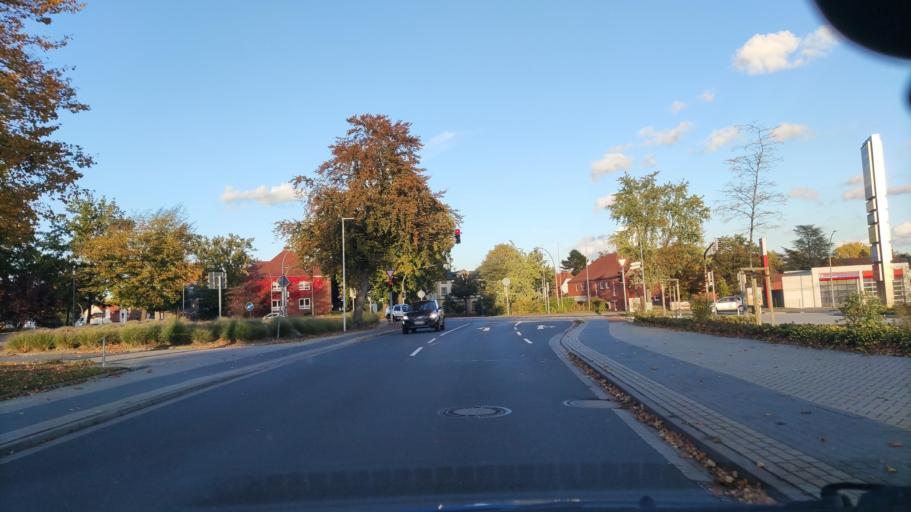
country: DE
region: Lower Saxony
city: Munster
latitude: 52.9893
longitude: 10.0799
